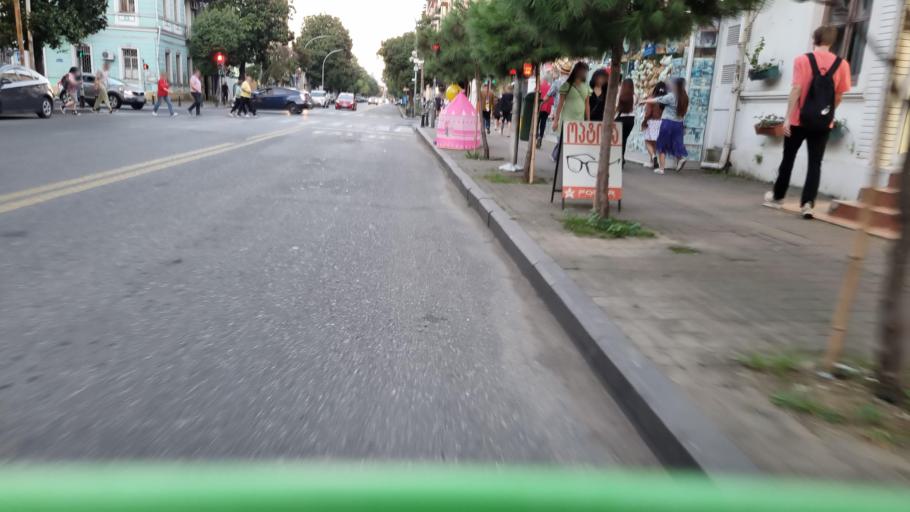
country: GE
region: Ajaria
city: Batumi
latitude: 41.6467
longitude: 41.6302
